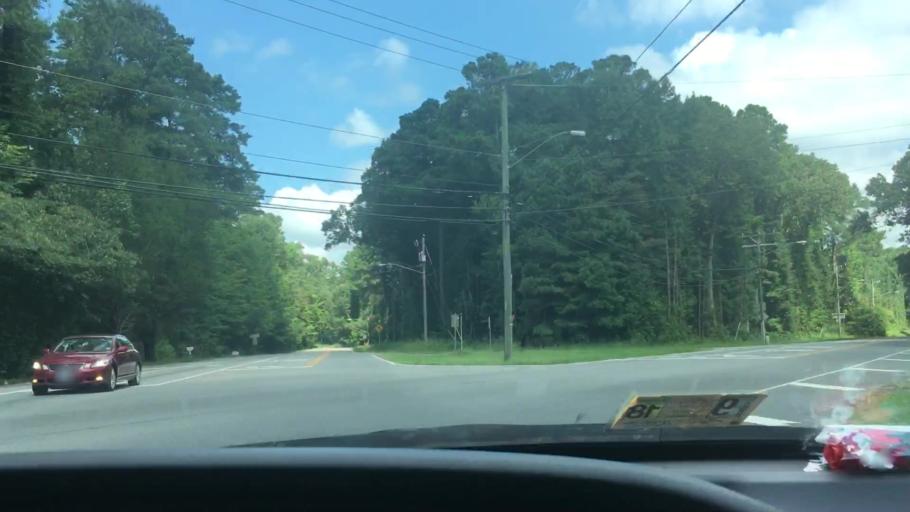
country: US
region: Virginia
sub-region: City of Virginia Beach
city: Virginia Beach
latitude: 36.7344
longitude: -76.0988
